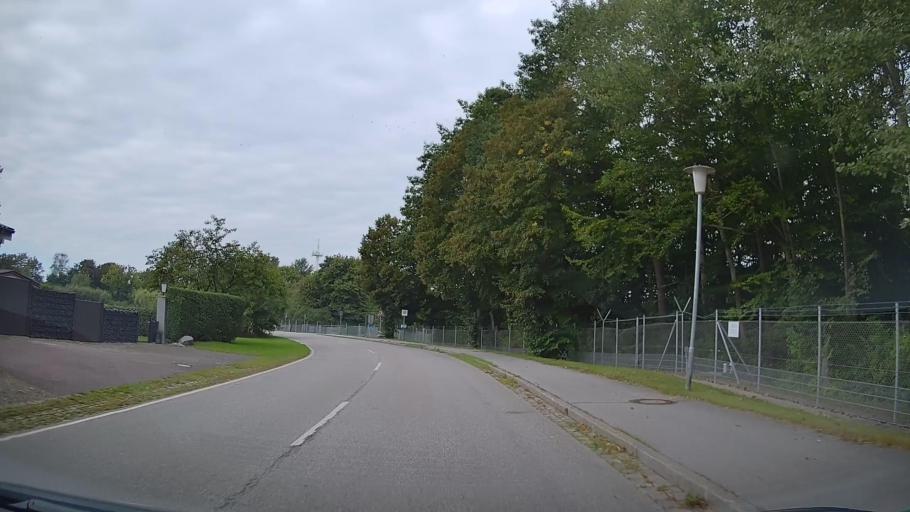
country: DE
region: Schleswig-Holstein
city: Panker
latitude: 54.3682
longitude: 10.5589
